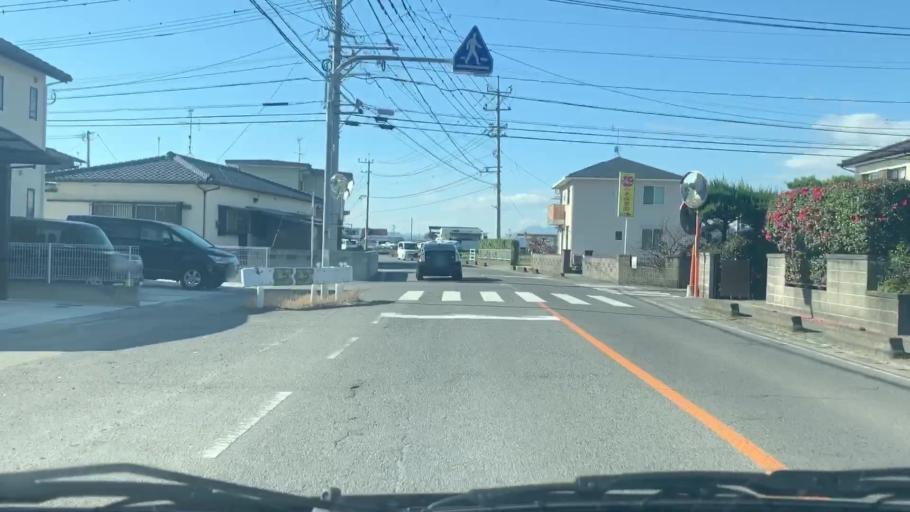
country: JP
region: Saga Prefecture
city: Saga-shi
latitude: 33.2905
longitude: 130.2751
